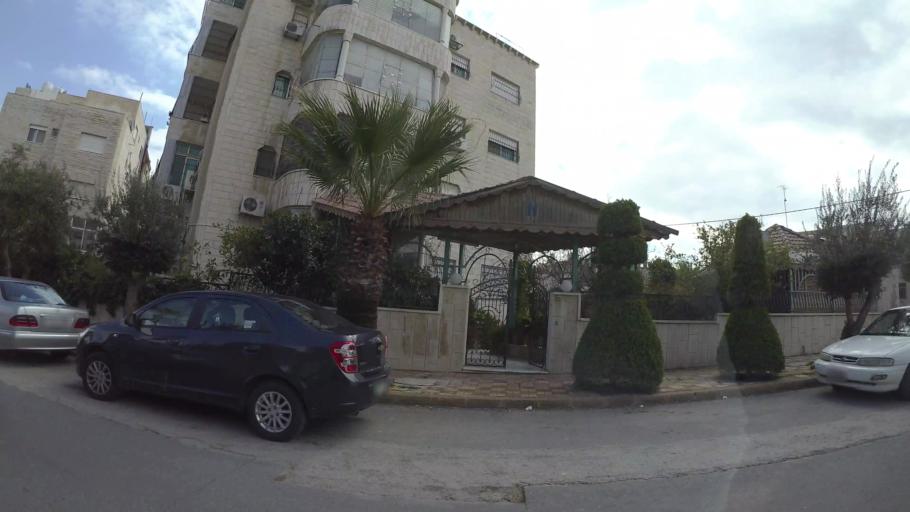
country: JO
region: Amman
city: Al Jubayhah
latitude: 31.9832
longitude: 35.8983
